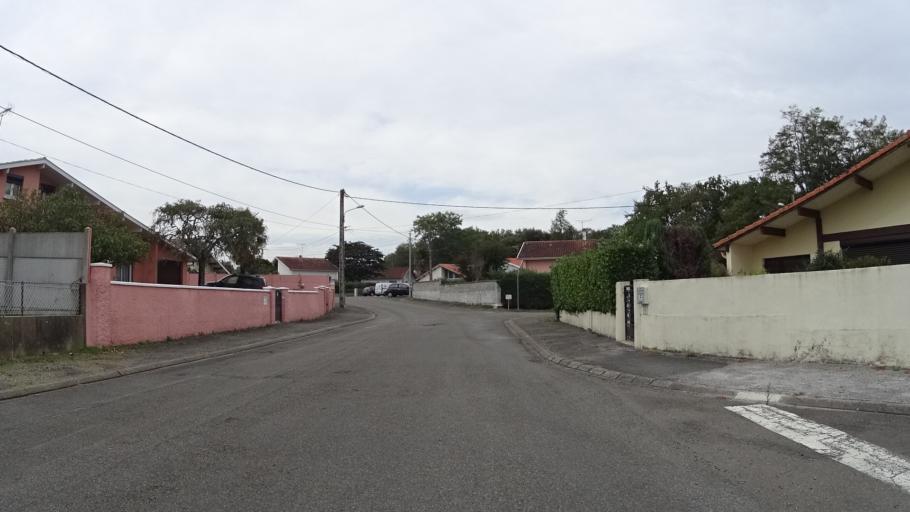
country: FR
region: Aquitaine
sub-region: Departement des Landes
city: Saint-Paul-les-Dax
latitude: 43.7301
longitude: -1.0732
